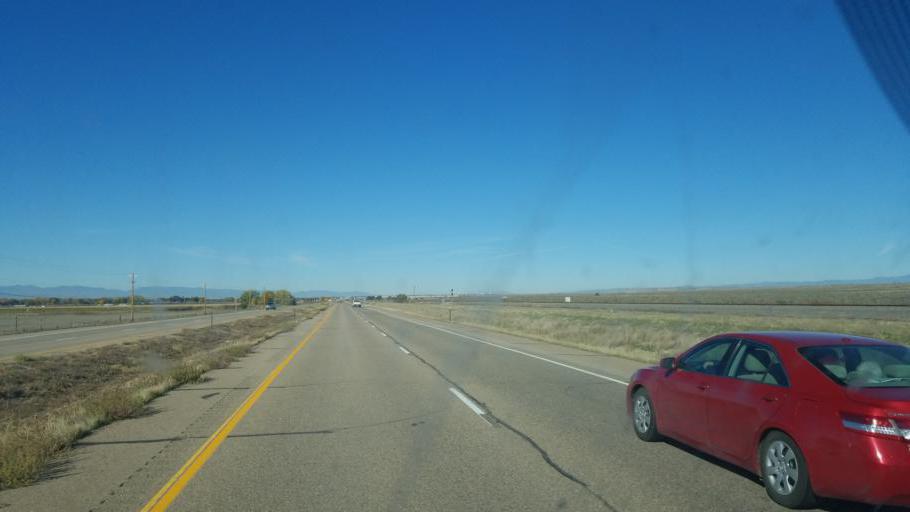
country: US
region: Colorado
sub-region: Pueblo County
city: Pueblo
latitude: 38.2708
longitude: -104.4140
